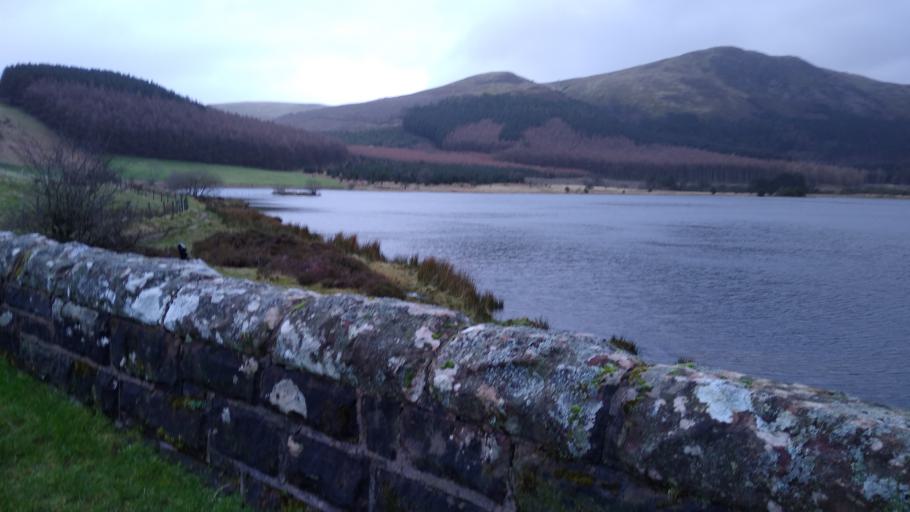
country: GB
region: England
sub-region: Cumbria
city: Frizington
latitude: 54.5631
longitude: -3.4055
